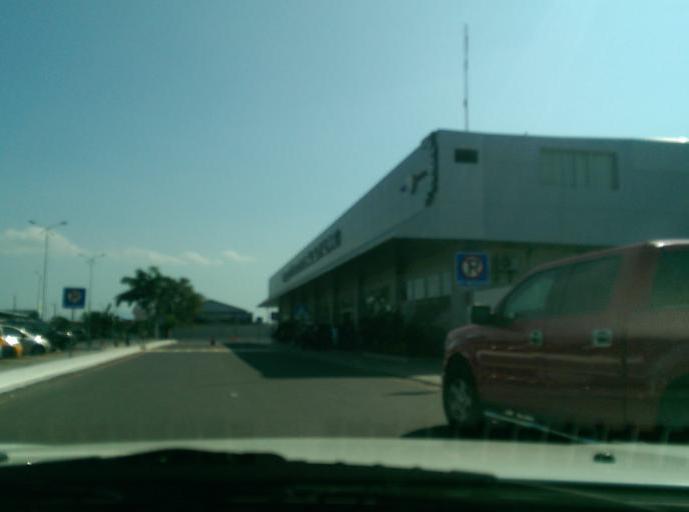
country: EC
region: Manabi
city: Manta
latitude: -0.9528
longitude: -80.6837
